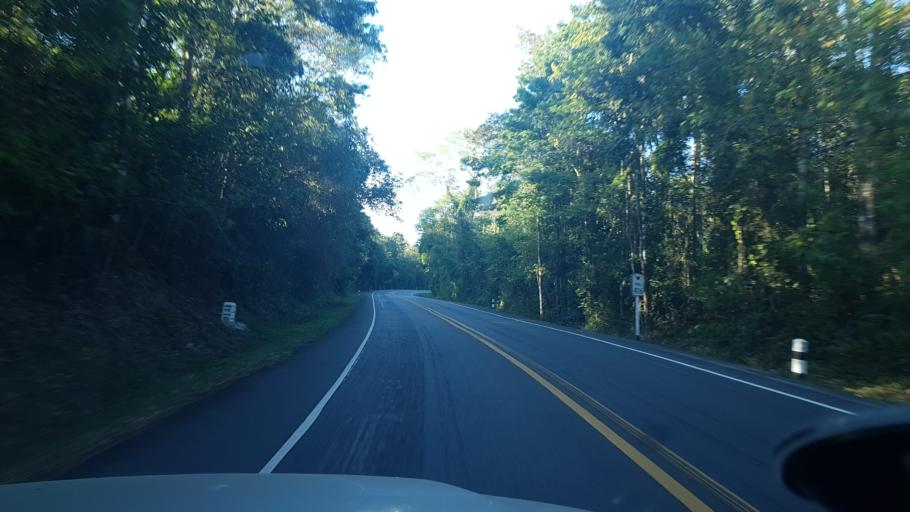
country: TH
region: Phetchabun
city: Nam Nao
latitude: 16.6993
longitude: 101.6412
